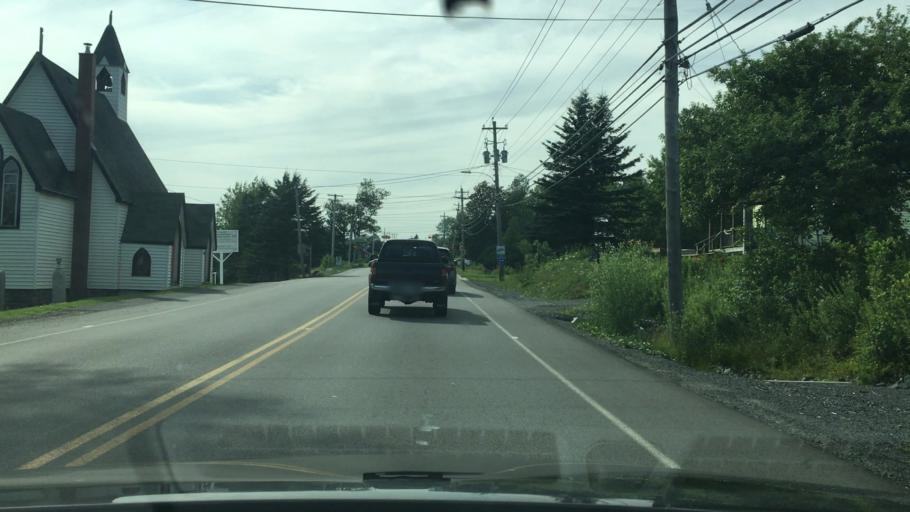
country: CA
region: Nova Scotia
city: Dartmouth
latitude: 44.7318
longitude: -63.7576
